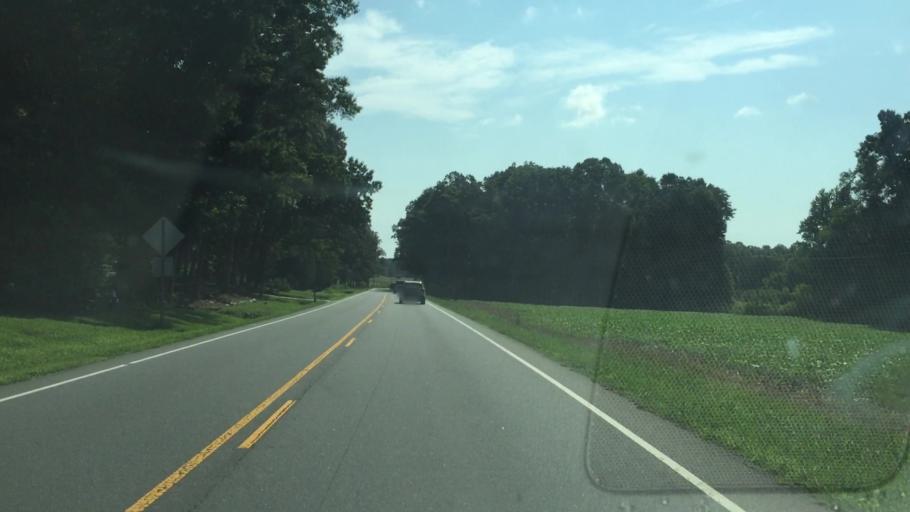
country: US
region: North Carolina
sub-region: Union County
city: Fairview
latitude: 35.1629
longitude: -80.5819
